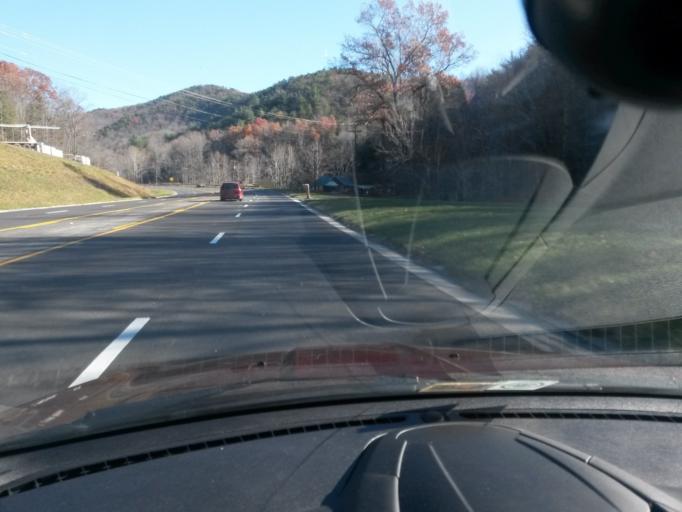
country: US
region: Virginia
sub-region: Patrick County
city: Stuart
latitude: 36.6563
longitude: -80.2804
